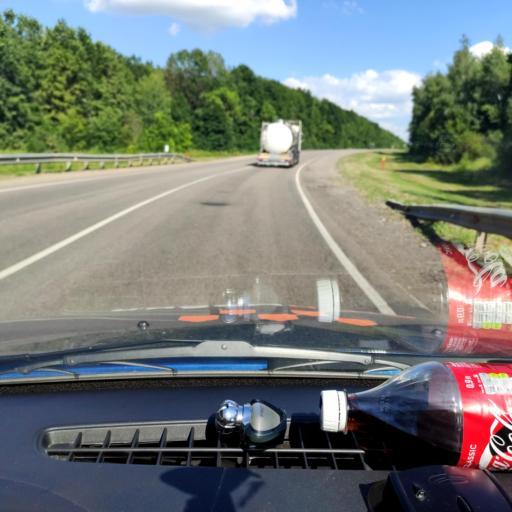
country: RU
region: Lipetsk
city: Kazaki
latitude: 52.6367
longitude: 38.3011
